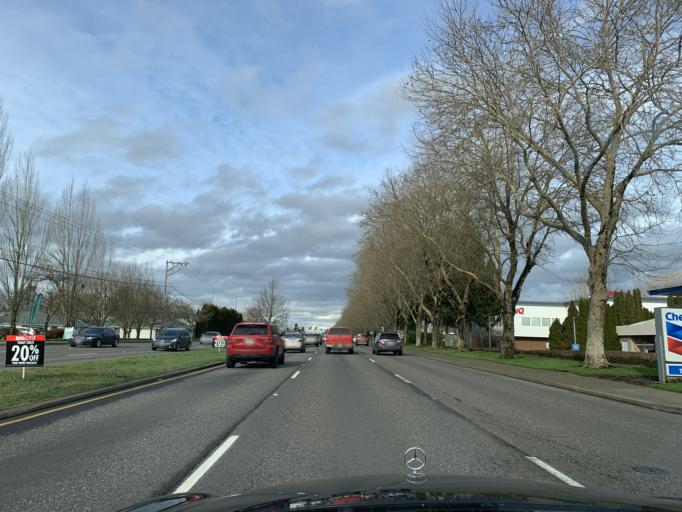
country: US
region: Washington
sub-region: Clark County
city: Mill Plain
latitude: 45.6020
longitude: -122.5038
